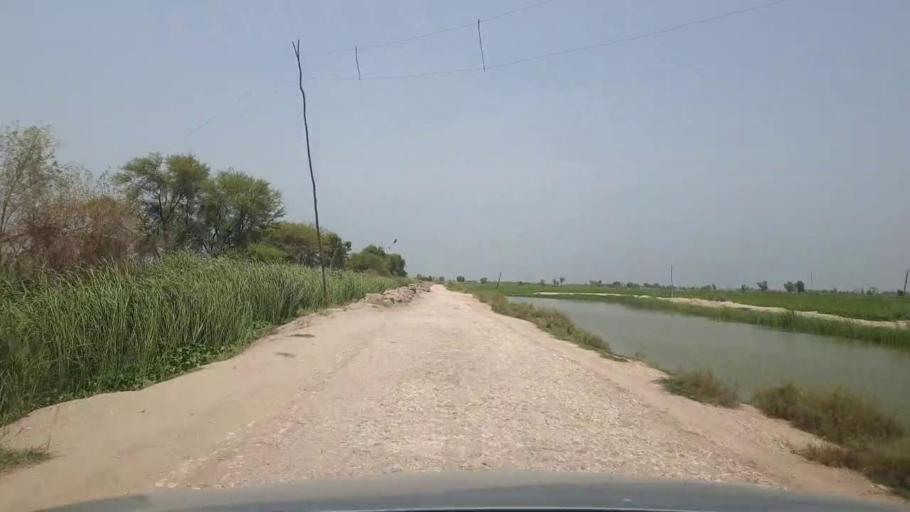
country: PK
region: Sindh
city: Garhi Yasin
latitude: 27.9253
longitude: 68.4335
